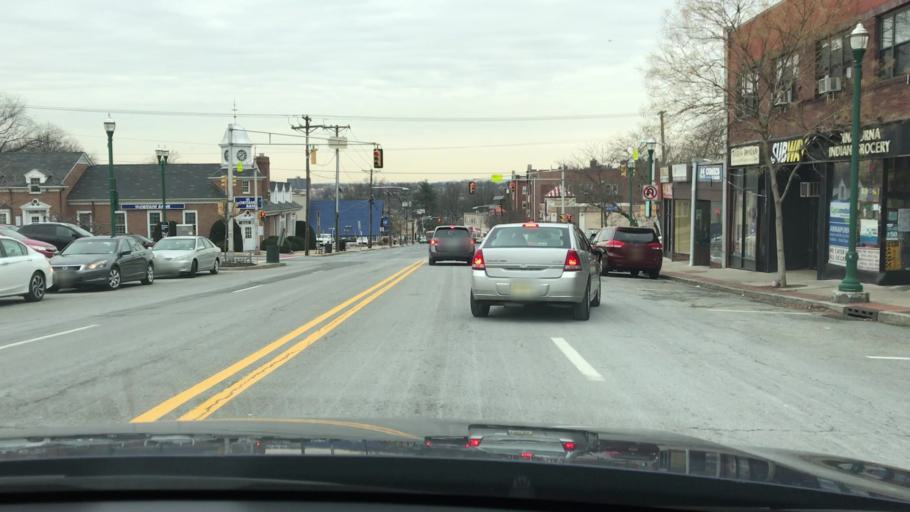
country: US
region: New Jersey
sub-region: Bergen County
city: Teaneck
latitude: 40.8902
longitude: -74.0251
